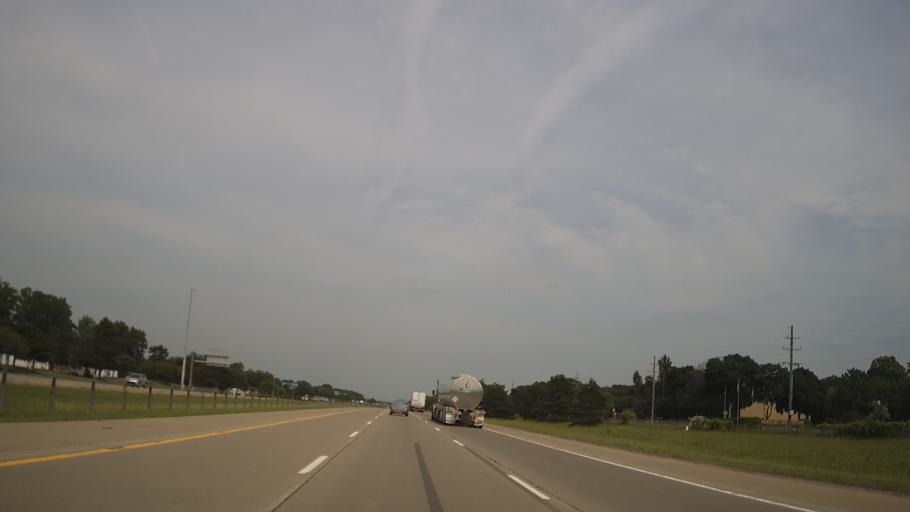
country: US
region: Michigan
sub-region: Wayne County
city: Belleville
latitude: 42.2188
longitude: -83.5223
